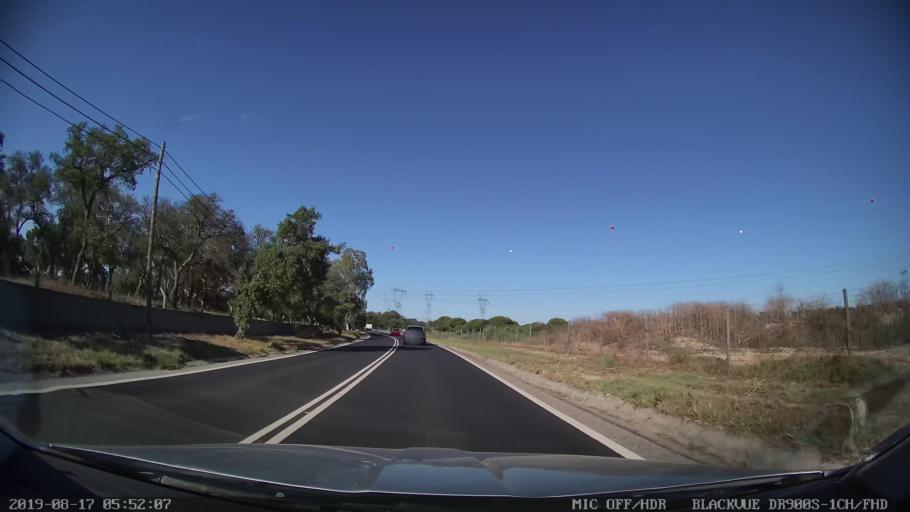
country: PT
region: Setubal
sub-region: Alcochete
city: Alcochete
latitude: 38.7719
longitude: -8.8898
